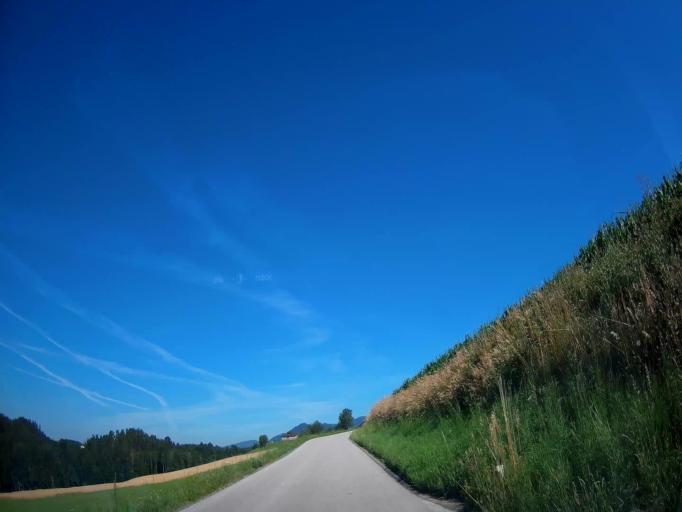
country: AT
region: Carinthia
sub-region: Politischer Bezirk Klagenfurt Land
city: Poggersdorf
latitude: 46.6646
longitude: 14.5347
